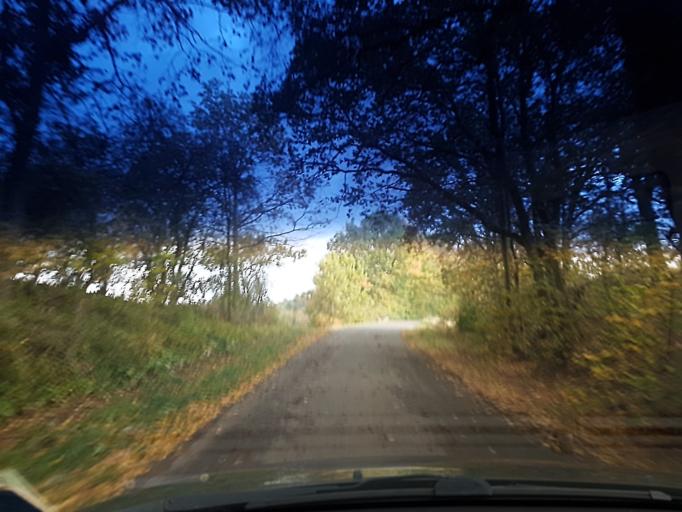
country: DE
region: Bavaria
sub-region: Regierungsbezirk Unterfranken
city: Geiselwind
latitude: 49.7649
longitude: 10.5316
